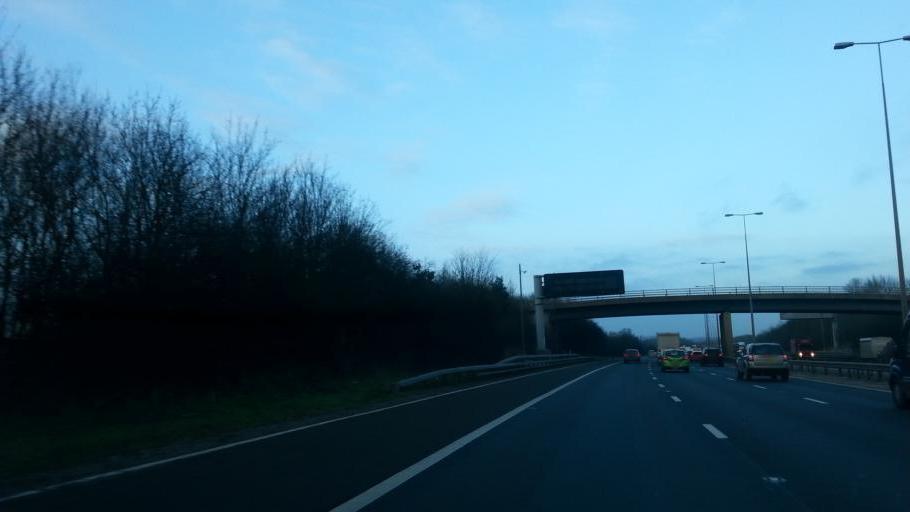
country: GB
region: England
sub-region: Worcestershire
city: Kempsey
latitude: 52.1318
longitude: -2.2007
